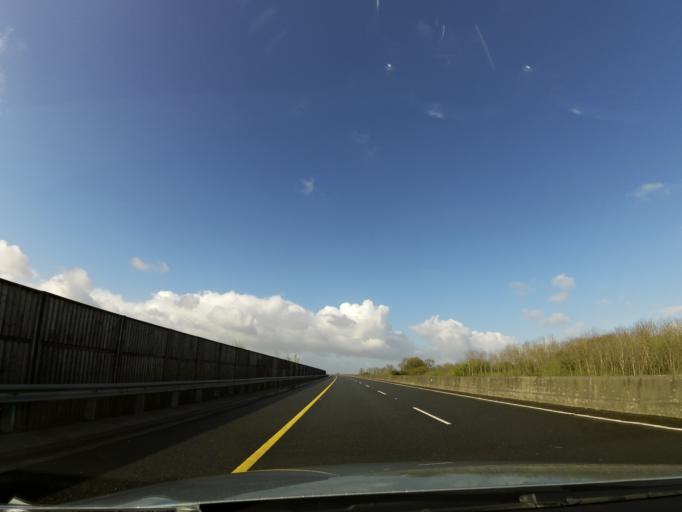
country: IE
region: Munster
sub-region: North Tipperary
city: Newport
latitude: 52.7372
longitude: -8.4487
